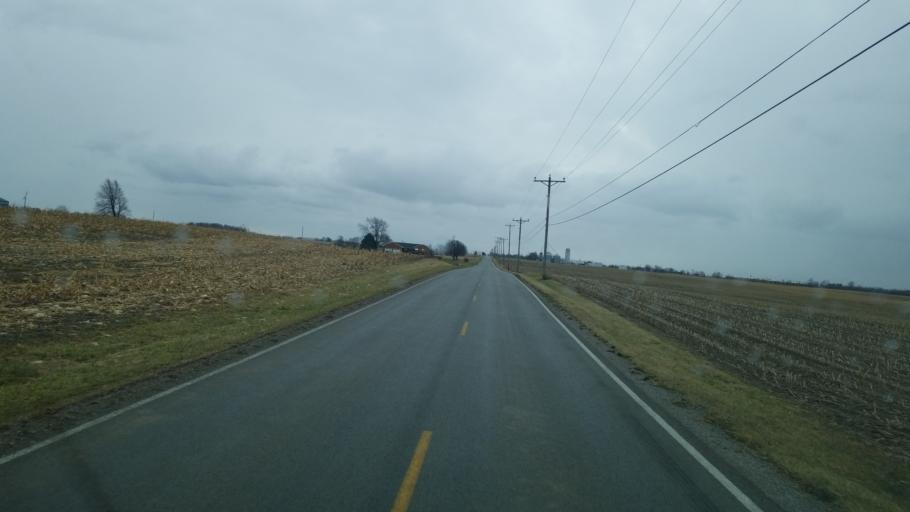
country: US
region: Ohio
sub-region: Hardin County
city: Kenton
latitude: 40.6727
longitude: -83.5761
